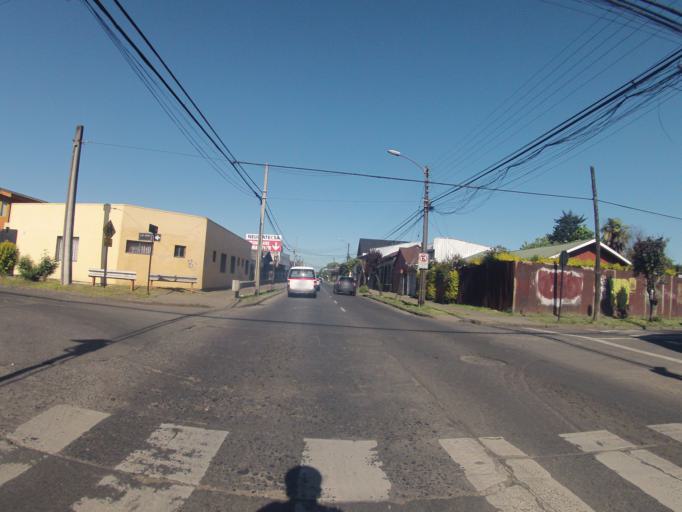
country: CL
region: Araucania
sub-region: Provincia de Cautin
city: Temuco
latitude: -38.7345
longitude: -72.5949
